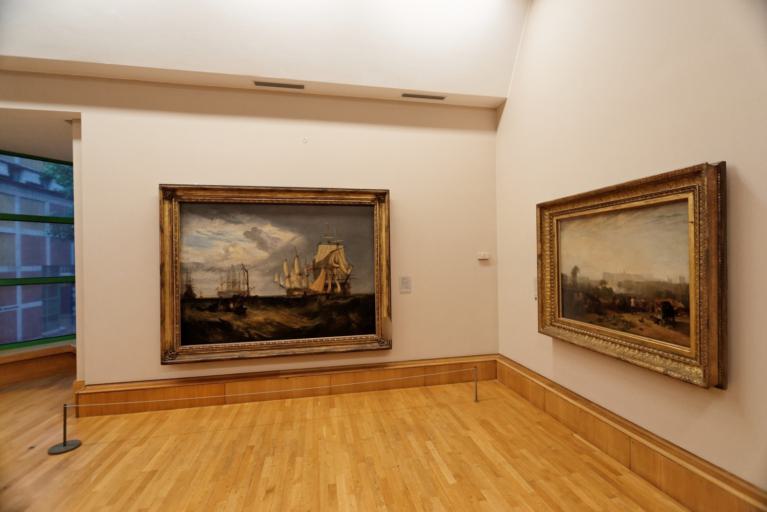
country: GB
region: England
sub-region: Greater London
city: City of Westminster
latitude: 51.4913
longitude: -0.1270
